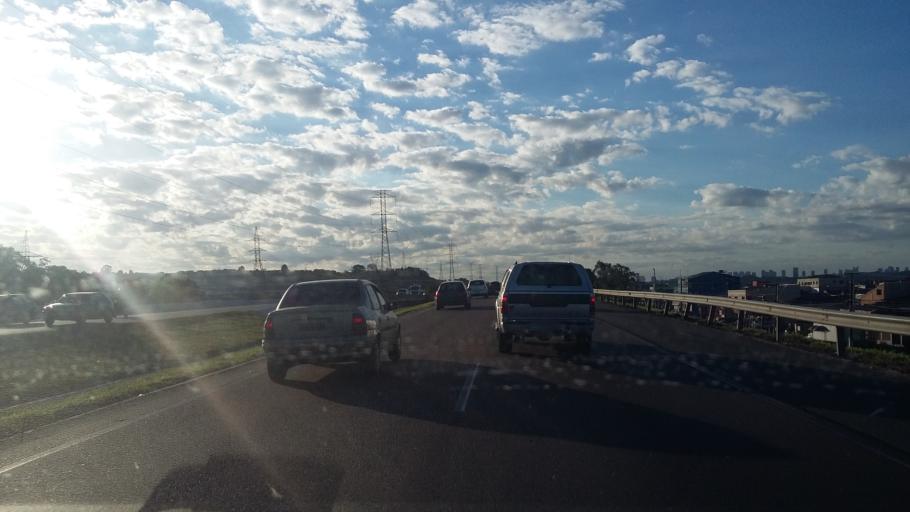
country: BR
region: Parana
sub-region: Araucaria
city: Araucaria
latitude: -25.5173
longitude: -49.3358
